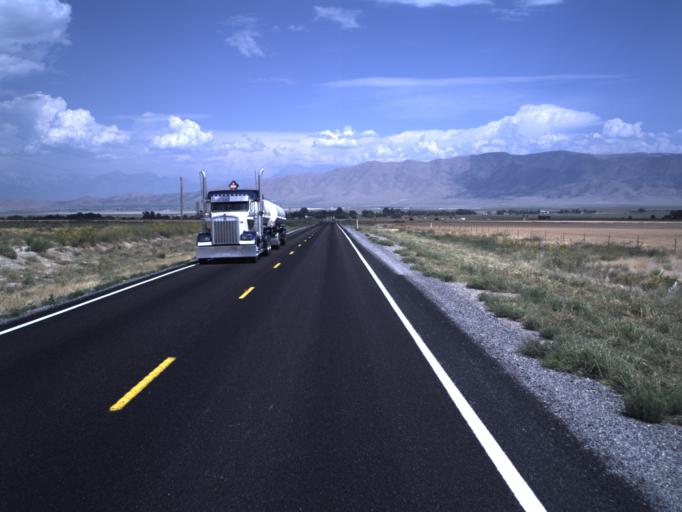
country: US
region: Utah
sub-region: Utah County
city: Eagle Mountain
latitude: 40.2517
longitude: -112.1170
